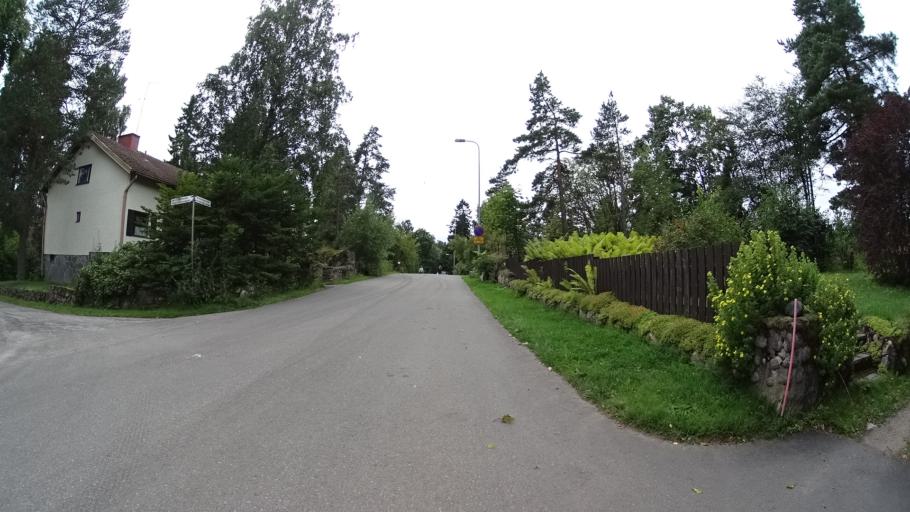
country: FI
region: Uusimaa
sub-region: Helsinki
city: Otaniemi
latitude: 60.1655
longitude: 24.7999
